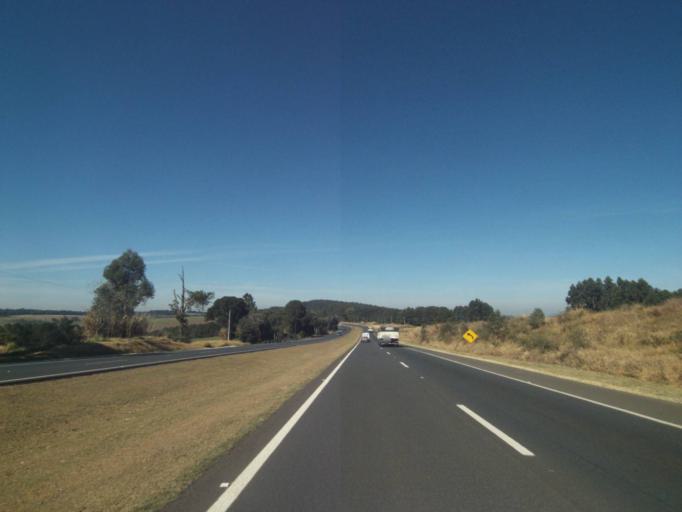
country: BR
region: Parana
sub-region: Carambei
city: Carambei
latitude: -24.8858
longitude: -50.4371
